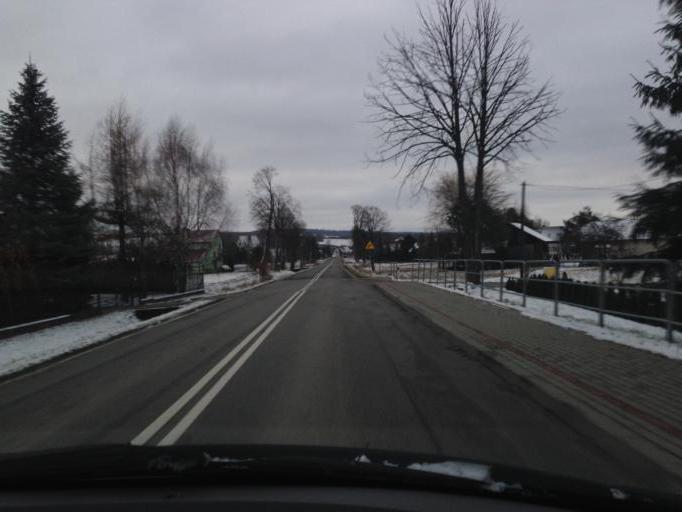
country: PL
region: Lesser Poland Voivodeship
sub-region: Powiat gorlicki
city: Moszczenica
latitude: 49.7049
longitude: 21.1251
